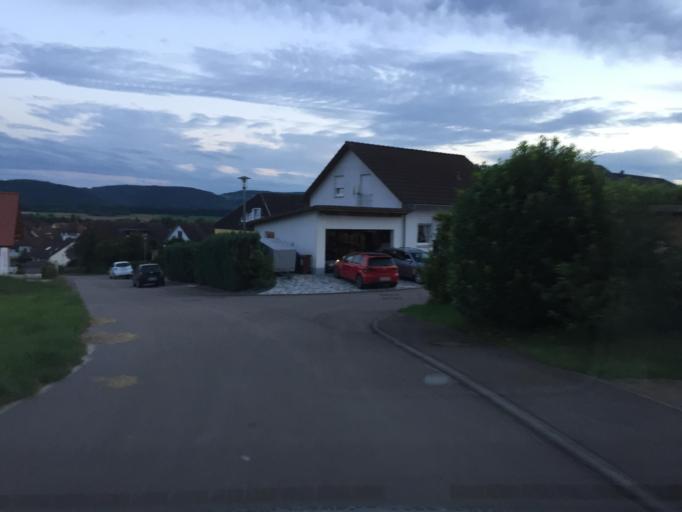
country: DE
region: Baden-Wuerttemberg
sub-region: Freiburg Region
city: Eggingen
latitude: 47.6643
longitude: 8.4237
